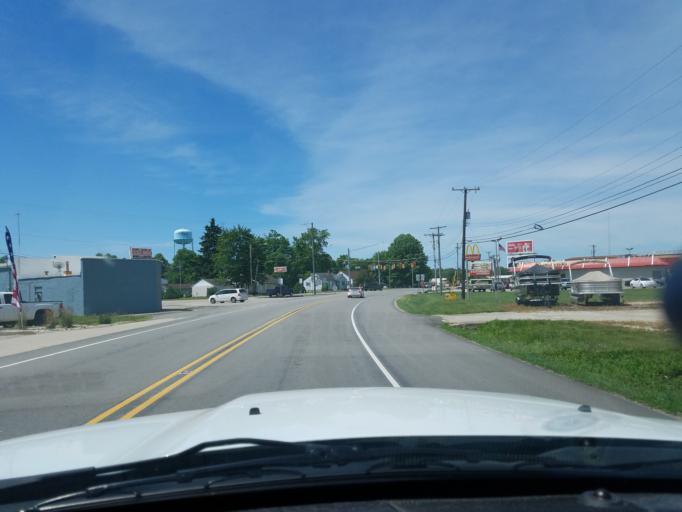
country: US
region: Indiana
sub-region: Delaware County
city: Albany
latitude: 40.3002
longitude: -85.2482
